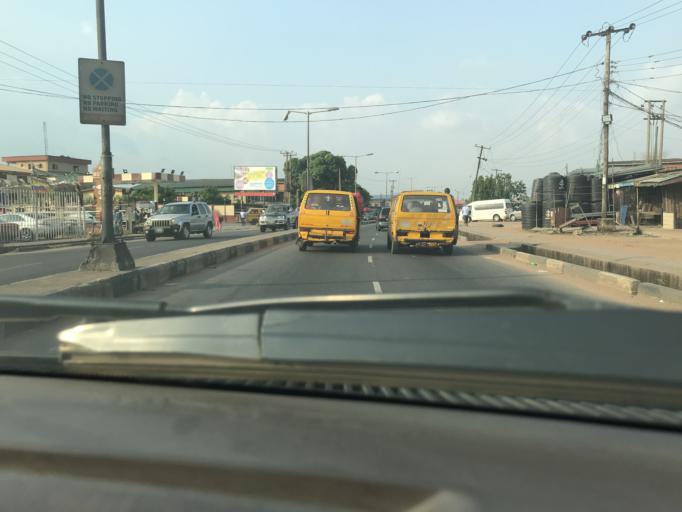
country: NG
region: Lagos
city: Agege
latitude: 6.5924
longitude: 3.2877
